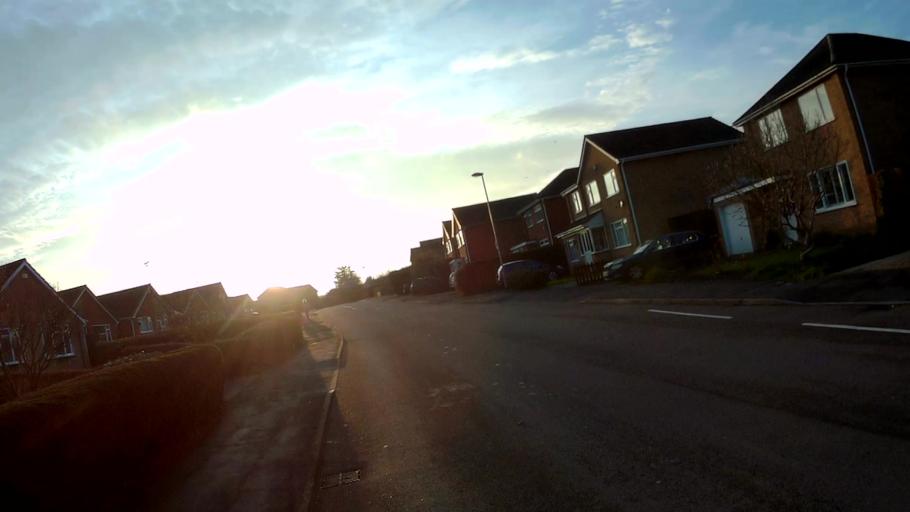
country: GB
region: England
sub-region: Lincolnshire
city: Bourne
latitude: 52.7737
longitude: -0.3880
